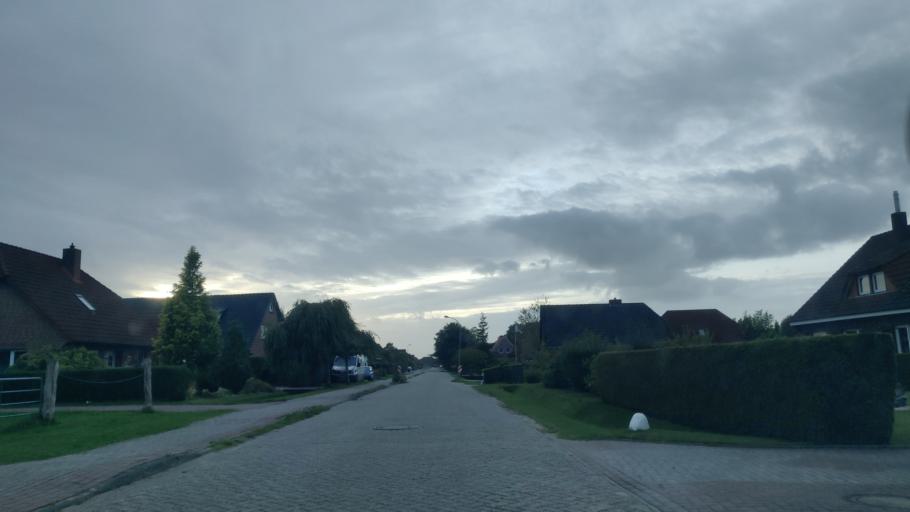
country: DE
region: Lower Saxony
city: Aurich
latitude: 53.4824
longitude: 7.4017
